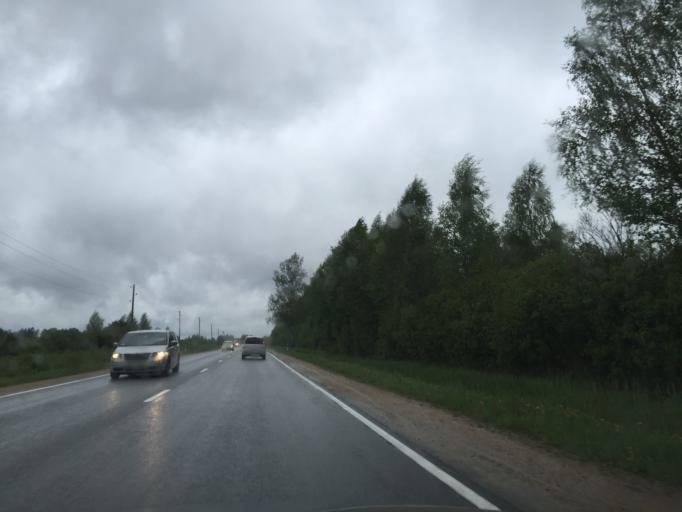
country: LV
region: Lielvarde
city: Lielvarde
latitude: 56.7244
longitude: 24.7654
